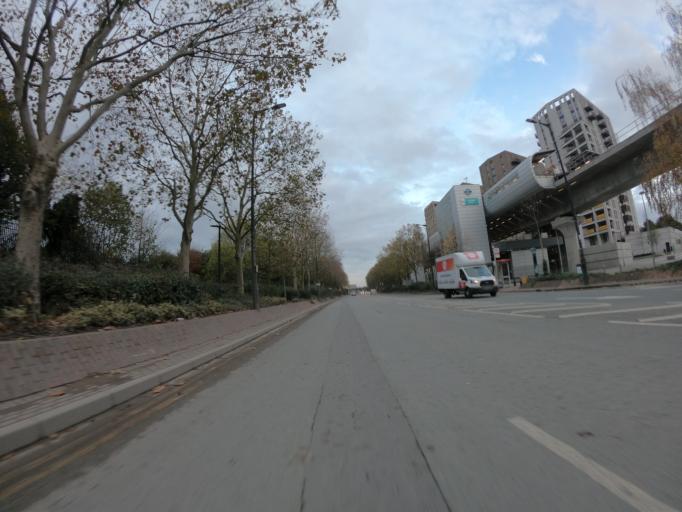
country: GB
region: England
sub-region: Greater London
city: Woolwich
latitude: 51.5025
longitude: 0.0321
